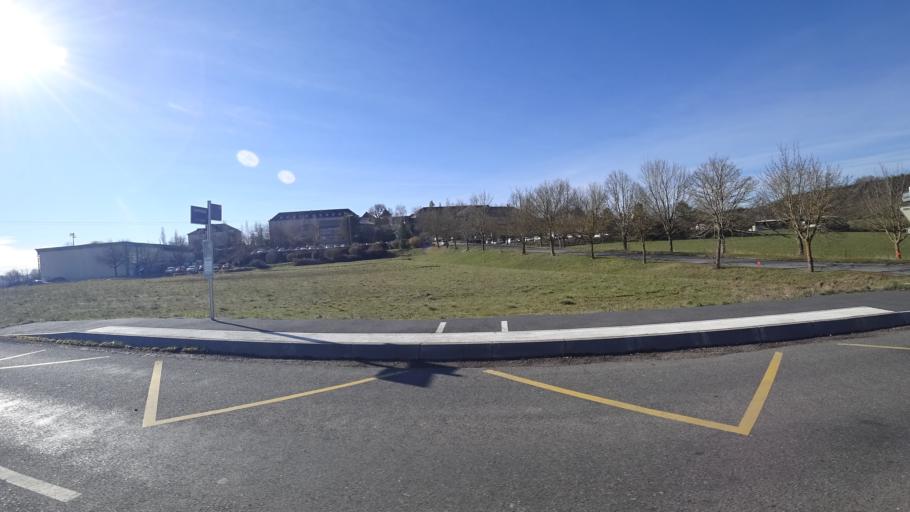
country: FR
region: Midi-Pyrenees
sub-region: Departement de l'Aveyron
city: Sebazac-Concoures
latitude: 44.3840
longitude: 2.5858
